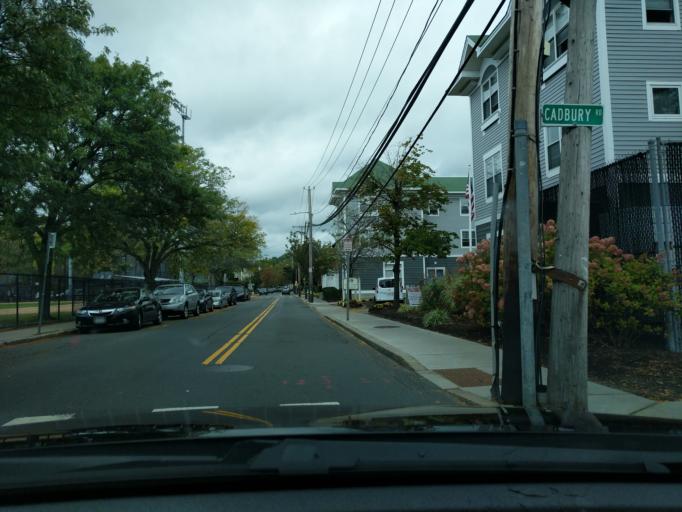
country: US
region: Massachusetts
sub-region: Middlesex County
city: Cambridge
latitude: 42.3871
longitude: -71.1315
